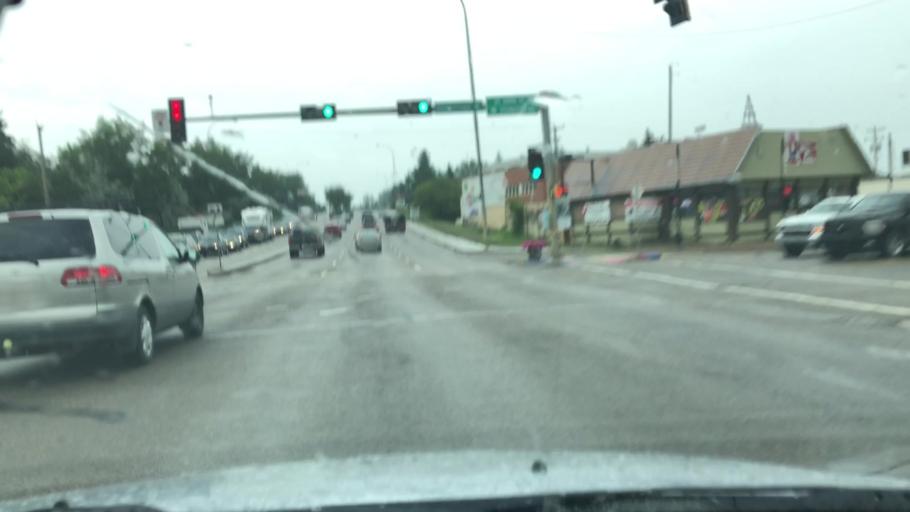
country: CA
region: Alberta
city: St. Albert
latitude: 53.6358
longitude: -113.6237
